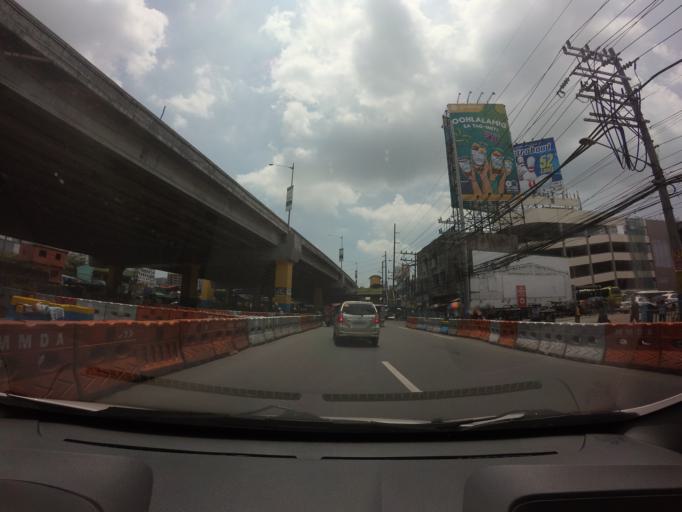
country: PH
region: Calabarzon
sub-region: Province of Laguna
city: San Pedro
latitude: 14.4154
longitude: 121.0457
